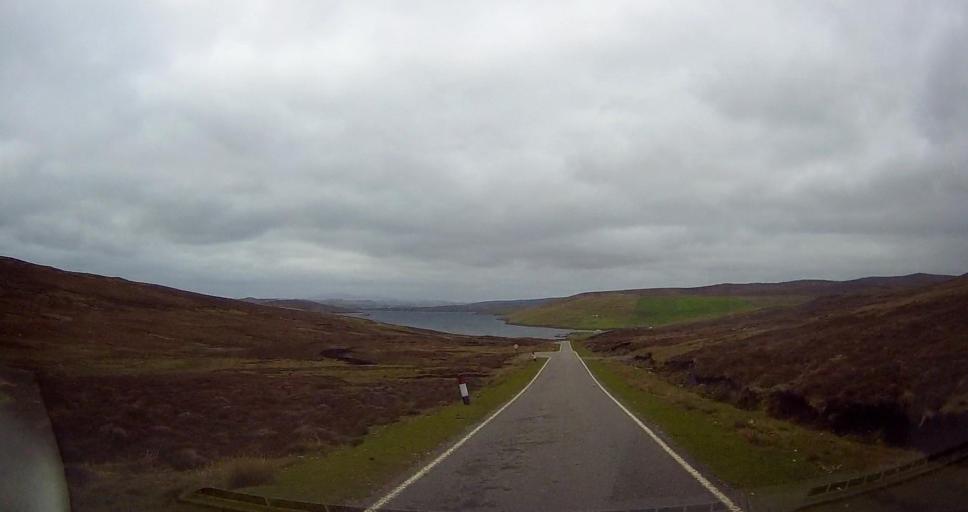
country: GB
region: Scotland
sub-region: Shetland Islands
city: Lerwick
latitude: 60.3251
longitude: -1.3392
